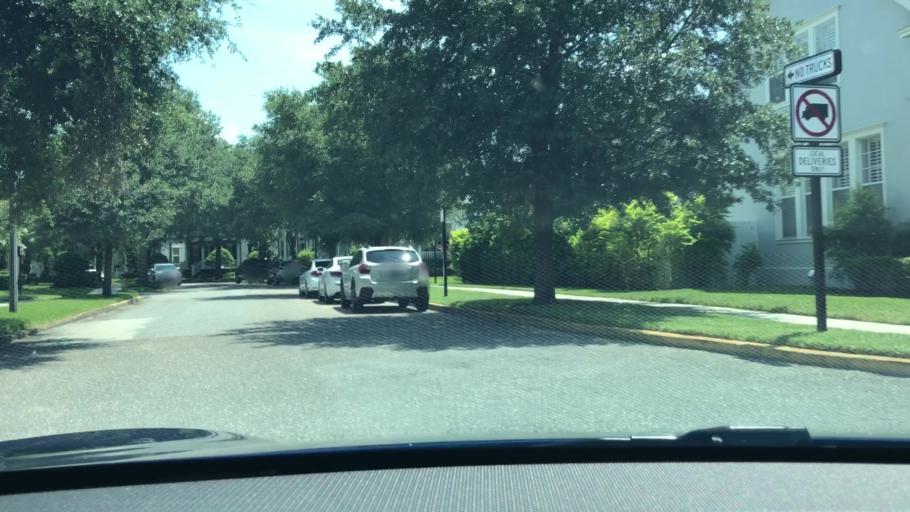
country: US
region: Florida
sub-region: Orange County
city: Winter Park
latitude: 28.5773
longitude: -81.3189
